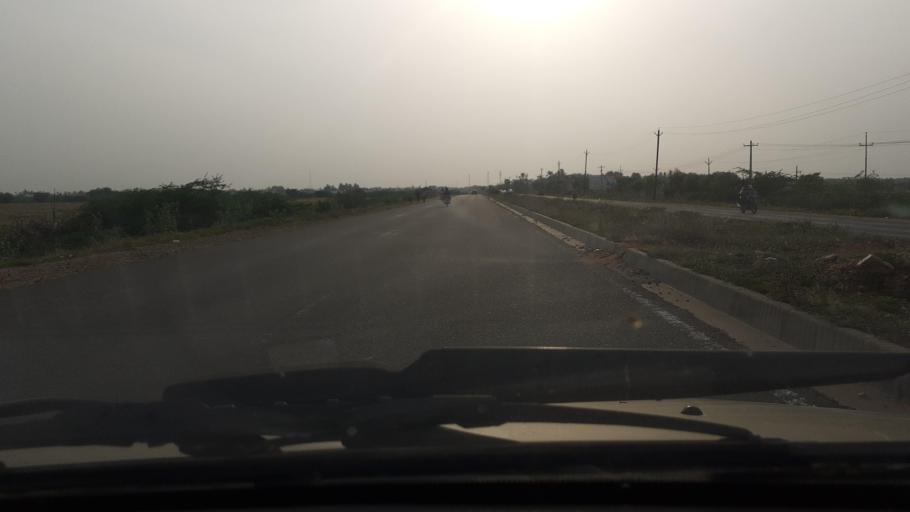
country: IN
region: Tamil Nadu
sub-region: Tirunelveli Kattabo
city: Tirunelveli
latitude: 8.7118
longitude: 77.8015
